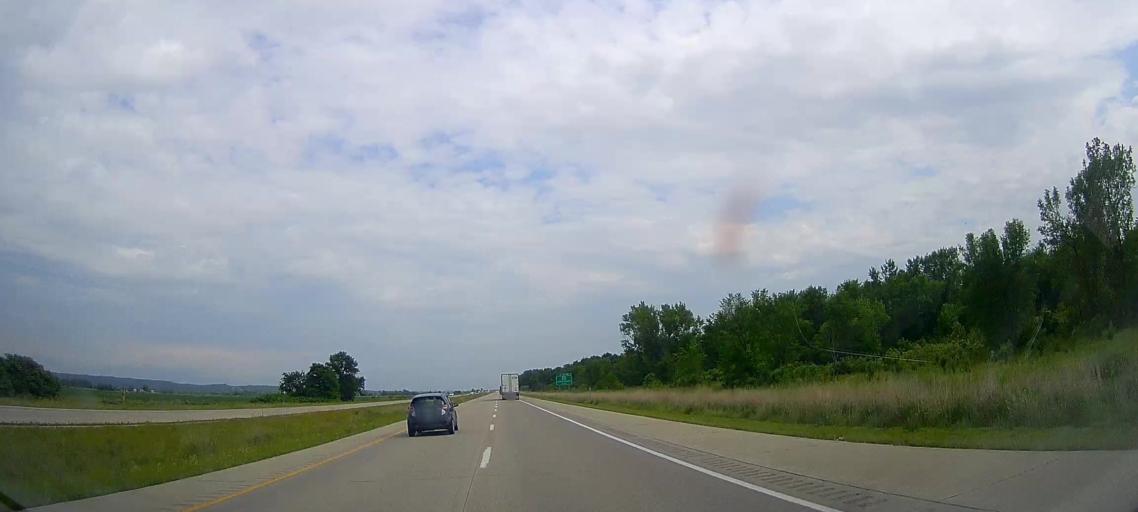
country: US
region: Nebraska
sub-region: Burt County
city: Tekamah
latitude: 41.8175
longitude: -96.0698
